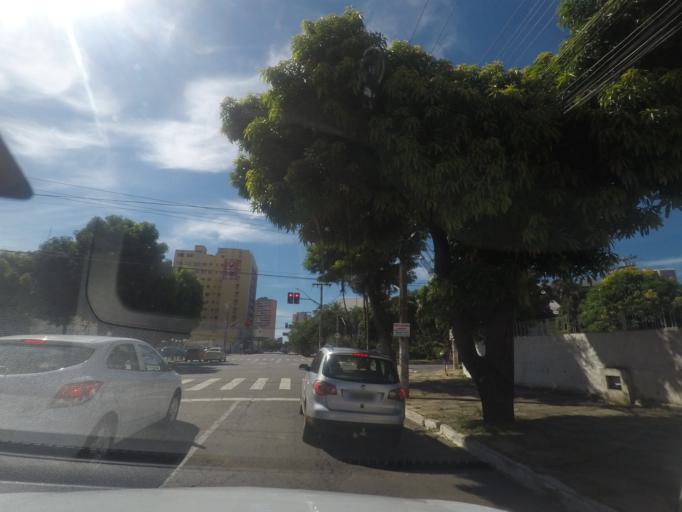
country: BR
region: Goias
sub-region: Goiania
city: Goiania
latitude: -16.6732
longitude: -49.2645
